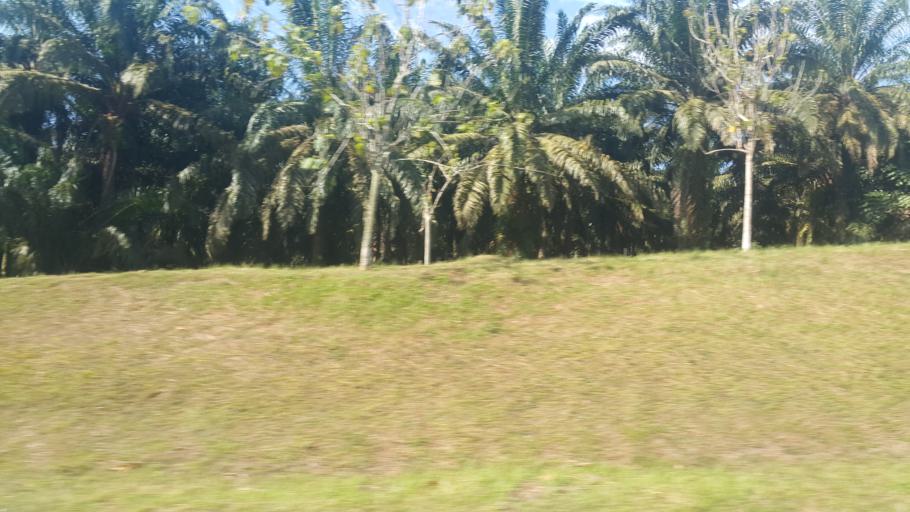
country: MY
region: Johor
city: Kelapa Sawit
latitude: 1.7273
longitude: 103.4257
